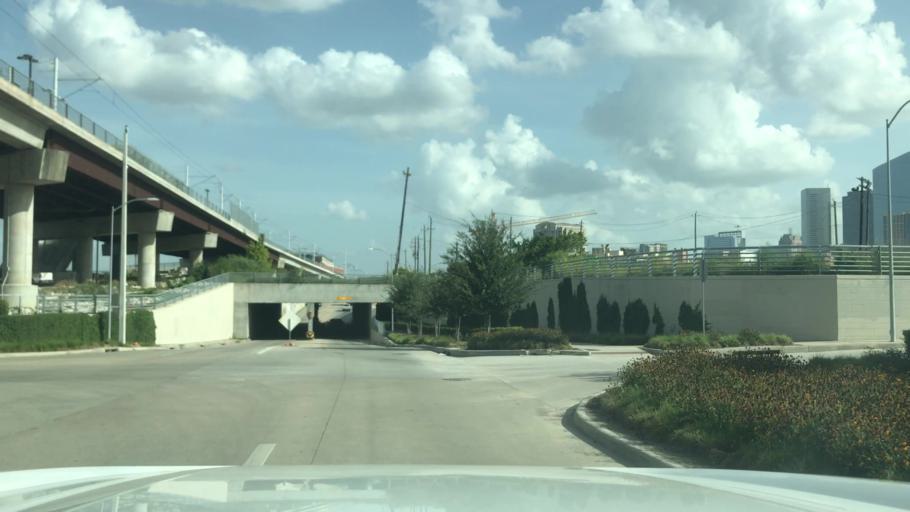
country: US
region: Texas
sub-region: Harris County
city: Houston
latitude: 29.7726
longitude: -95.3600
